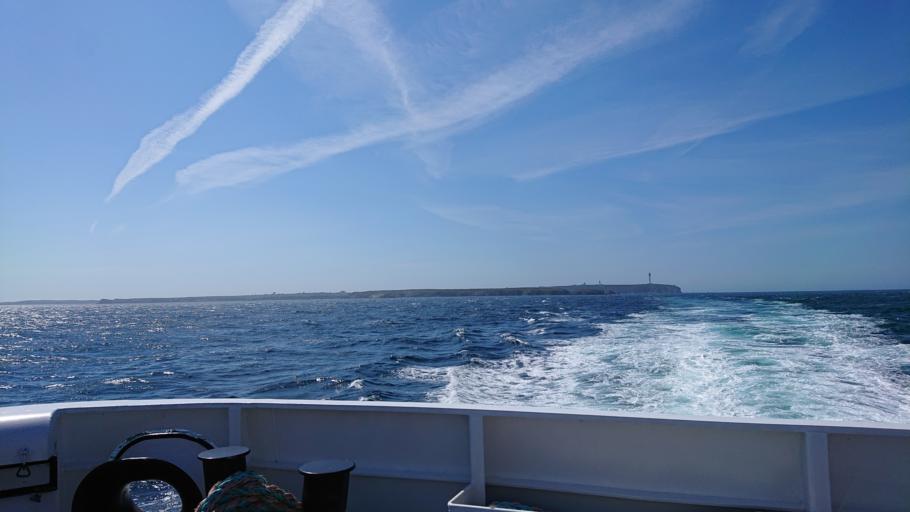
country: FR
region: Brittany
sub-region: Departement du Finistere
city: Porspoder
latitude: 48.4534
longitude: -5.0111
